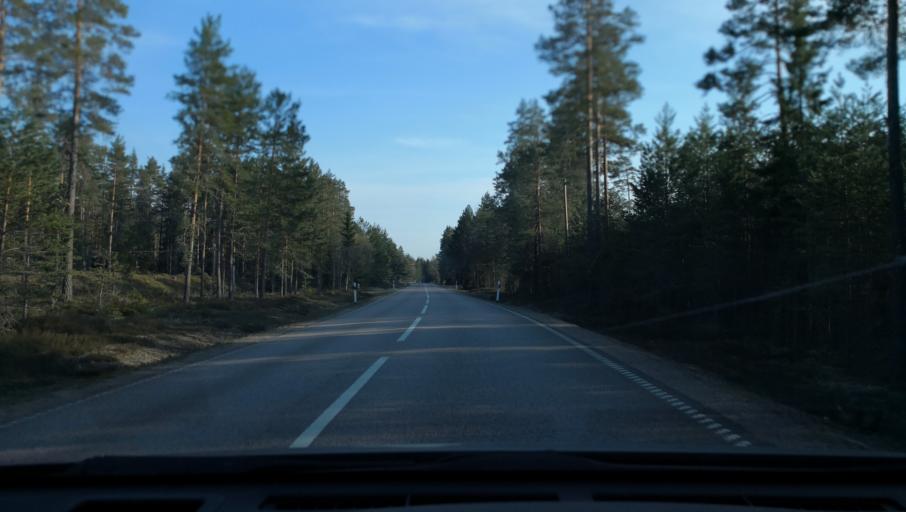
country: SE
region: Uppsala
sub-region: Heby Kommun
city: Tarnsjo
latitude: 60.0839
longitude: 16.8802
